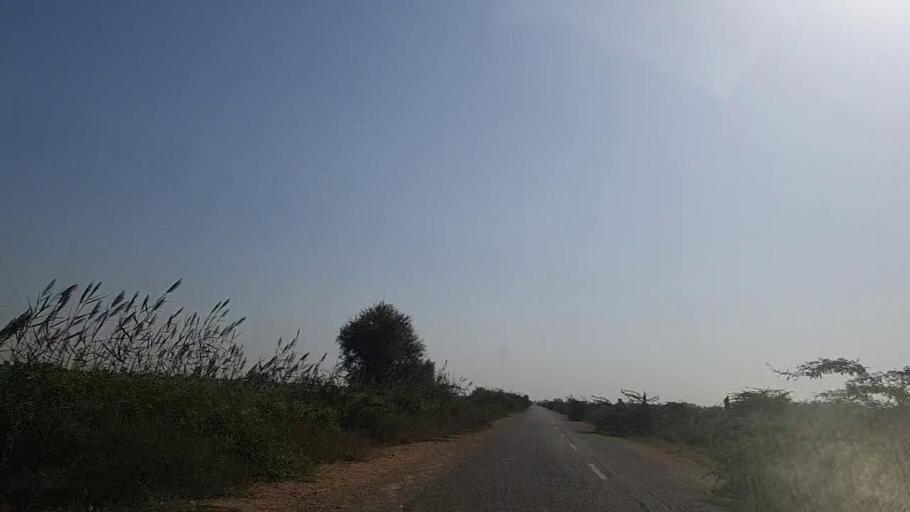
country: PK
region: Sindh
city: Jati
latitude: 24.4414
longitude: 68.2615
